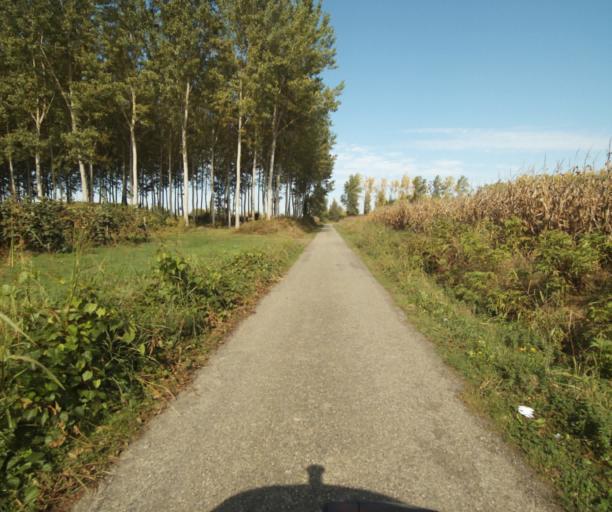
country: FR
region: Midi-Pyrenees
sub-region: Departement du Tarn-et-Garonne
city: Finhan
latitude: 43.9072
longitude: 1.2157
